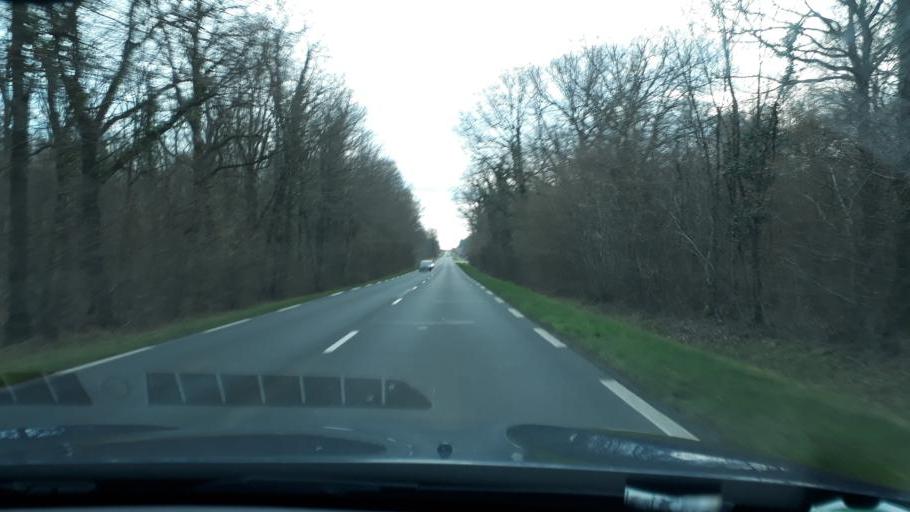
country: FR
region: Centre
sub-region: Departement du Loiret
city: Chilleurs-aux-Bois
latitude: 48.0445
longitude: 2.1245
